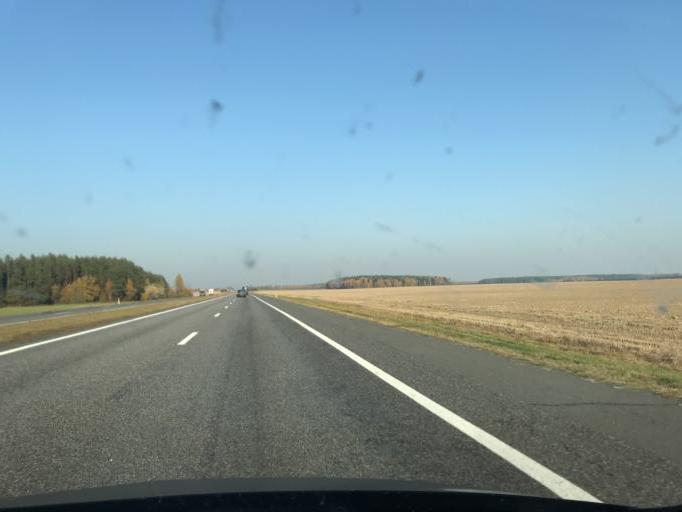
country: BY
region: Minsk
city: Haradzyeya
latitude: 53.3628
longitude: 26.4800
